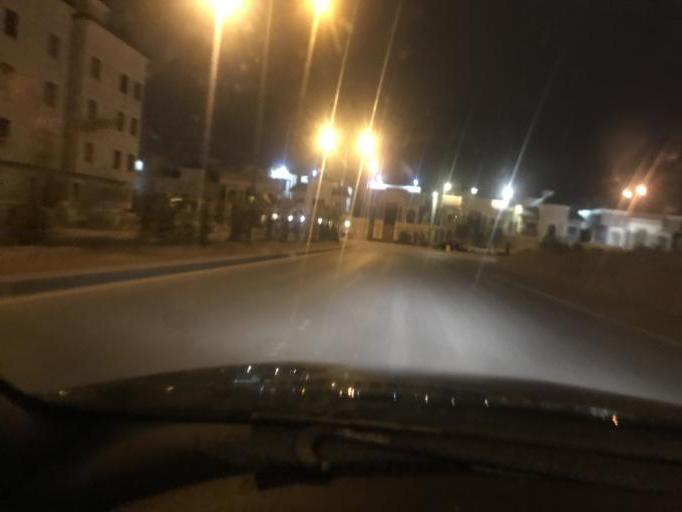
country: SA
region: Ar Riyad
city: Riyadh
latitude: 24.8055
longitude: 46.6820
